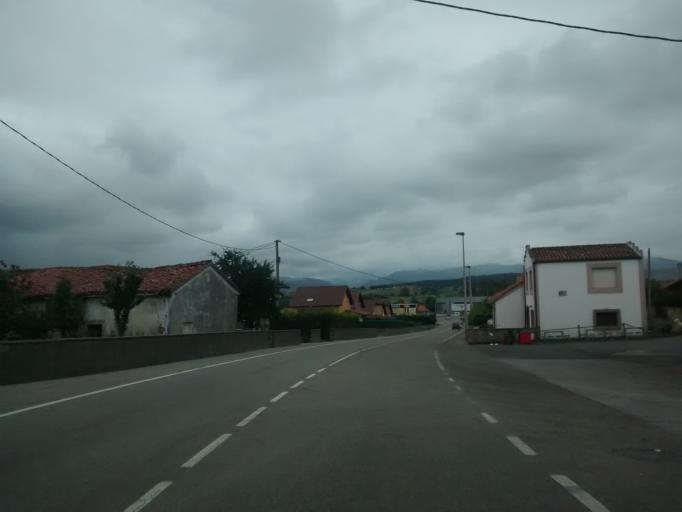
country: ES
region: Cantabria
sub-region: Provincia de Cantabria
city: Suances
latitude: 43.3999
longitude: -4.0483
